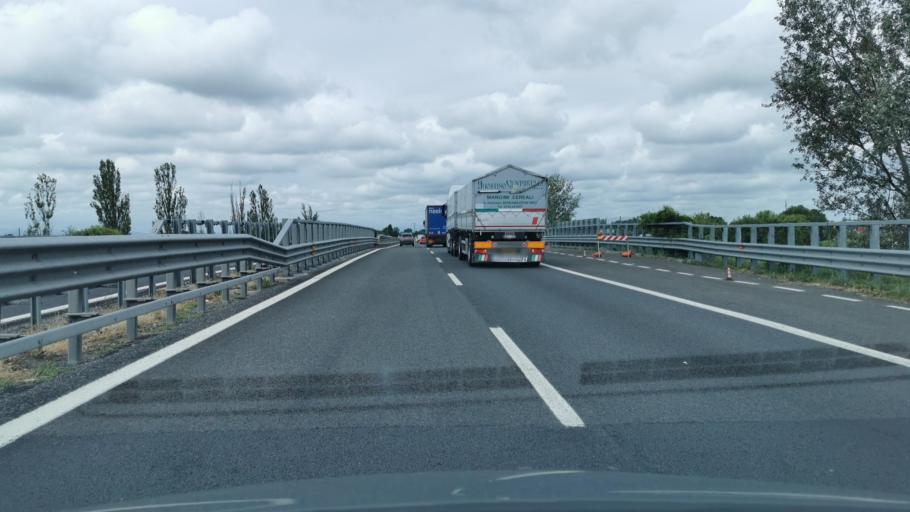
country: IT
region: Emilia-Romagna
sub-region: Provincia di Ravenna
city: Bagnacavallo
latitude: 44.4055
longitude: 11.9894
